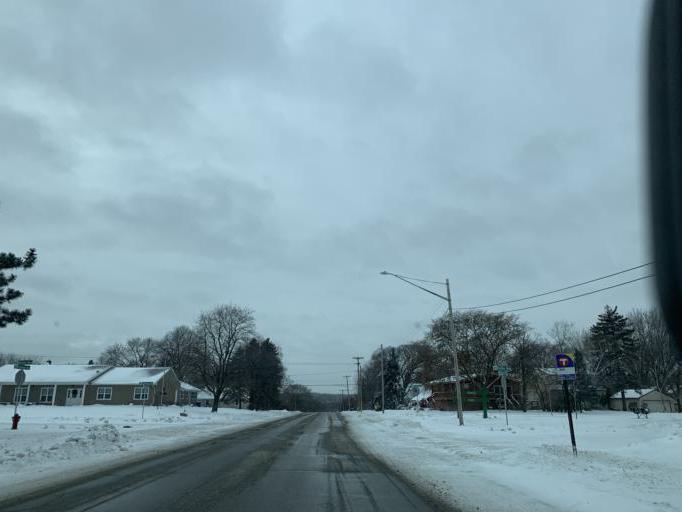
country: US
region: Minnesota
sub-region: Washington County
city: Saint Paul Park
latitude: 44.8367
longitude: -92.9882
